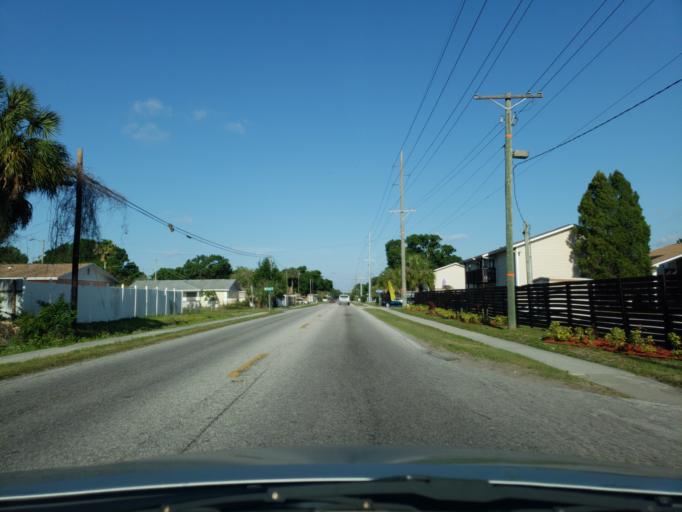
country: US
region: Florida
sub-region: Hillsborough County
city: Palm River-Clair Mel
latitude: 27.9412
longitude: -82.3734
